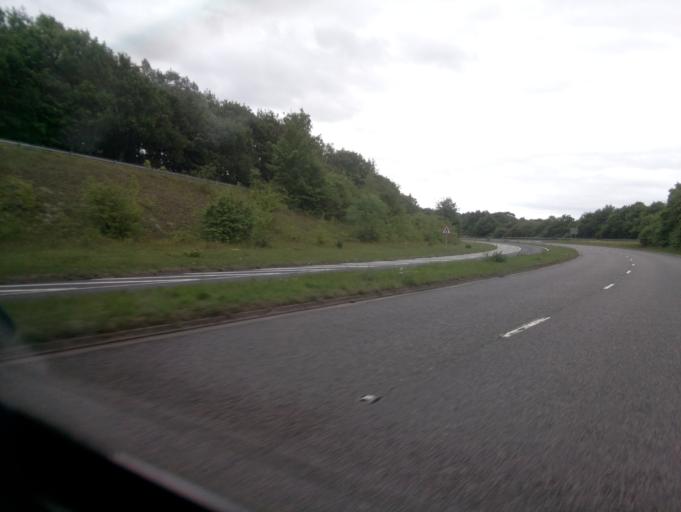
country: GB
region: England
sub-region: Worcestershire
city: Droitwich
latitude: 52.2624
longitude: -2.1782
